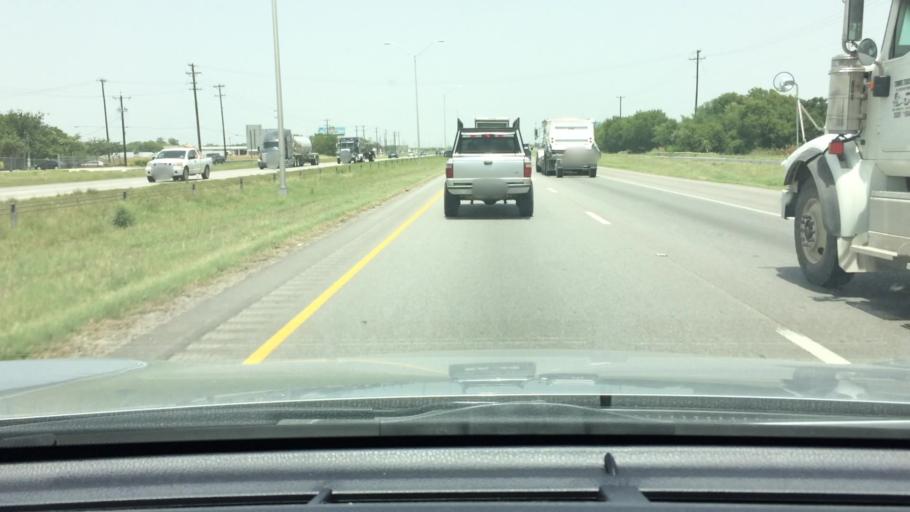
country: US
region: Texas
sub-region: Bexar County
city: China Grove
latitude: 29.4150
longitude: -98.3892
